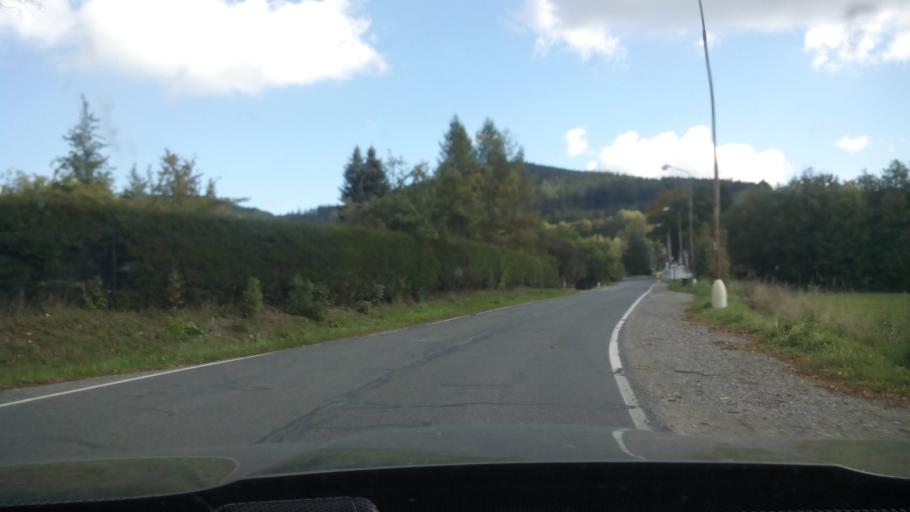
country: CZ
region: Plzensky
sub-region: Okres Klatovy
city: Kasperske Hory
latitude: 49.1468
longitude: 13.5669
